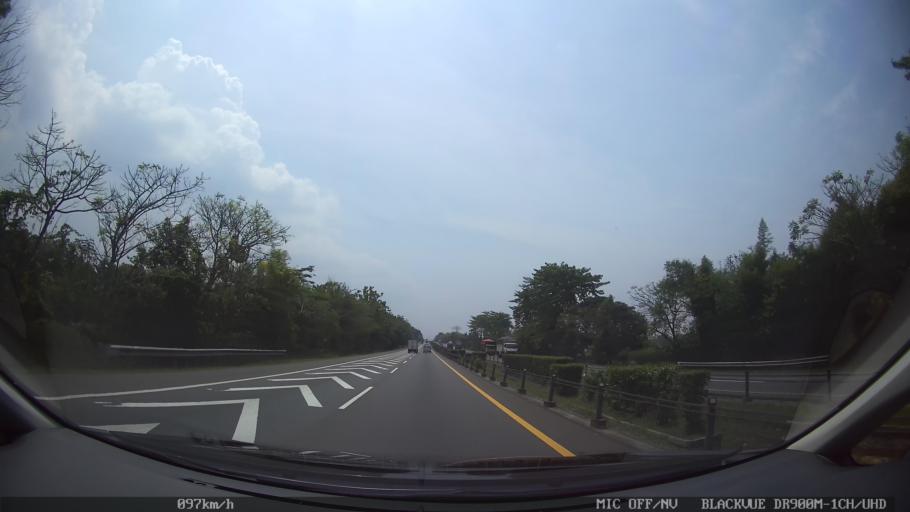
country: ID
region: Banten
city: Serang
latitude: -6.0808
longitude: 106.1334
